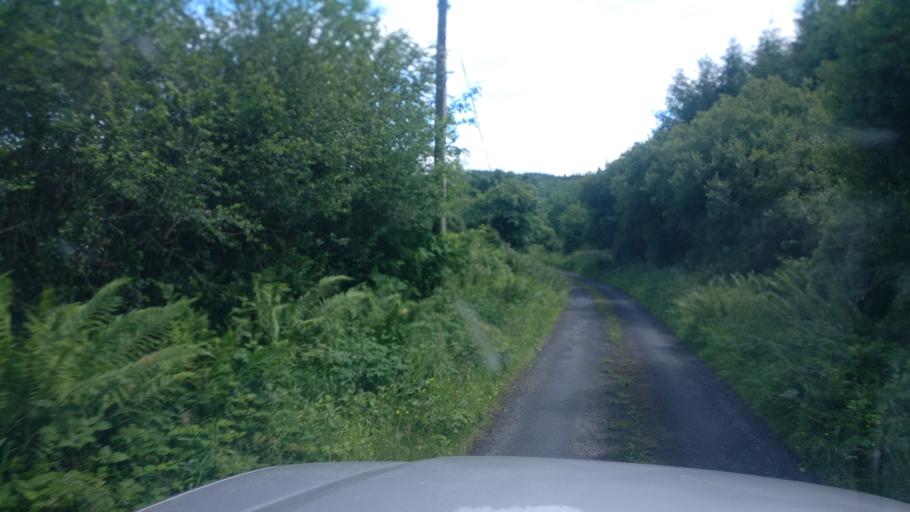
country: IE
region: Connaught
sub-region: County Galway
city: Gort
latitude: 53.0698
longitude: -8.7034
